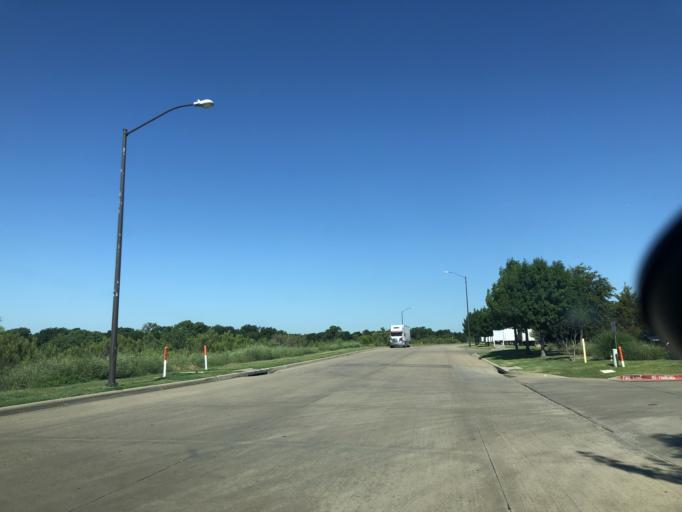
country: US
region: Texas
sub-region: Tarrant County
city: Euless
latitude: 32.8097
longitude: -97.0392
